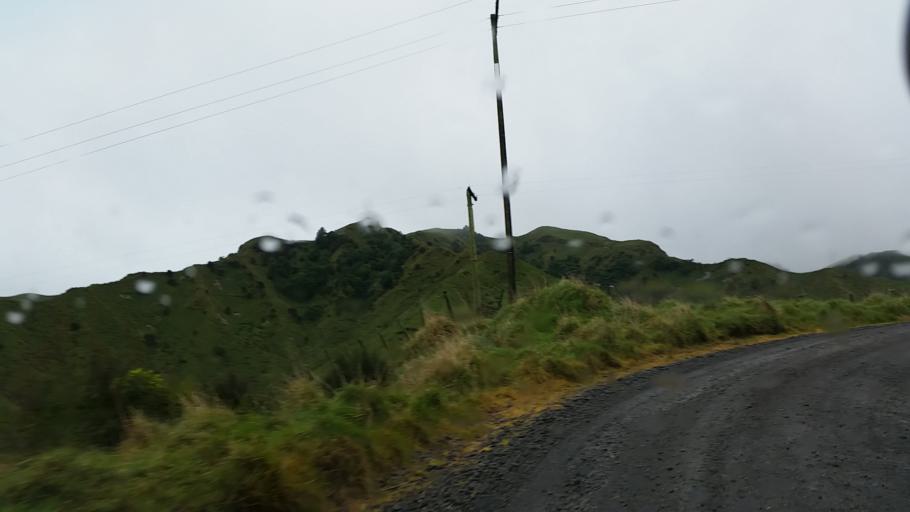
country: NZ
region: Taranaki
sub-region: South Taranaki District
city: Eltham
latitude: -39.4770
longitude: 174.4091
